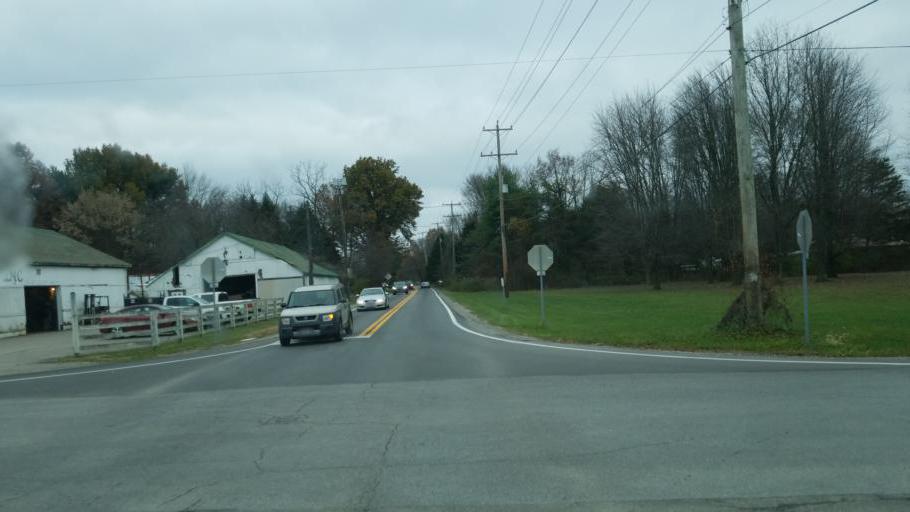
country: US
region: Ohio
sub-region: Franklin County
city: New Albany
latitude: 40.1140
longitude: -82.8382
